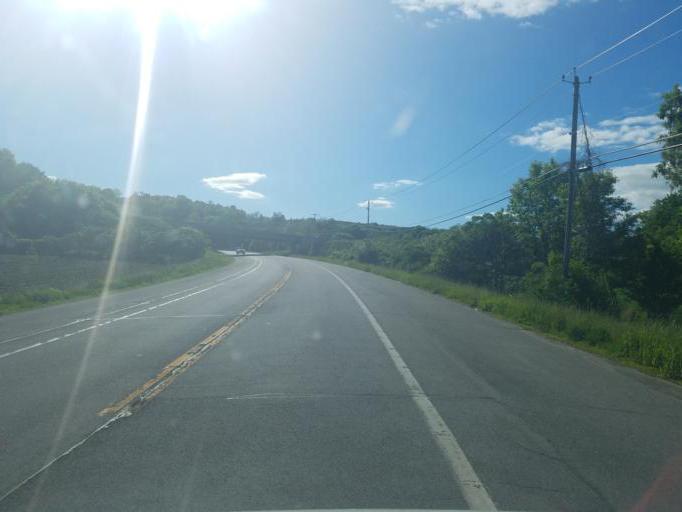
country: US
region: New York
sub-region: Herkimer County
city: Little Falls
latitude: 43.0207
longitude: -74.8169
